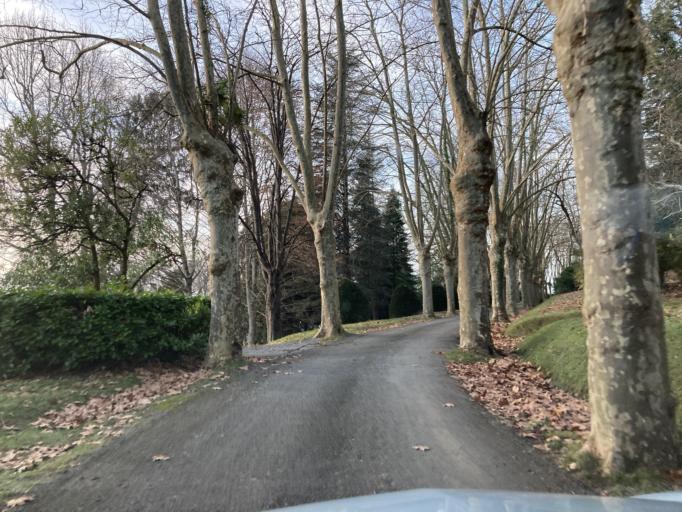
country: FR
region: Aquitaine
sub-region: Departement des Pyrenees-Atlantiques
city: Oloron-Sainte-Marie
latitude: 43.1912
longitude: -0.5995
